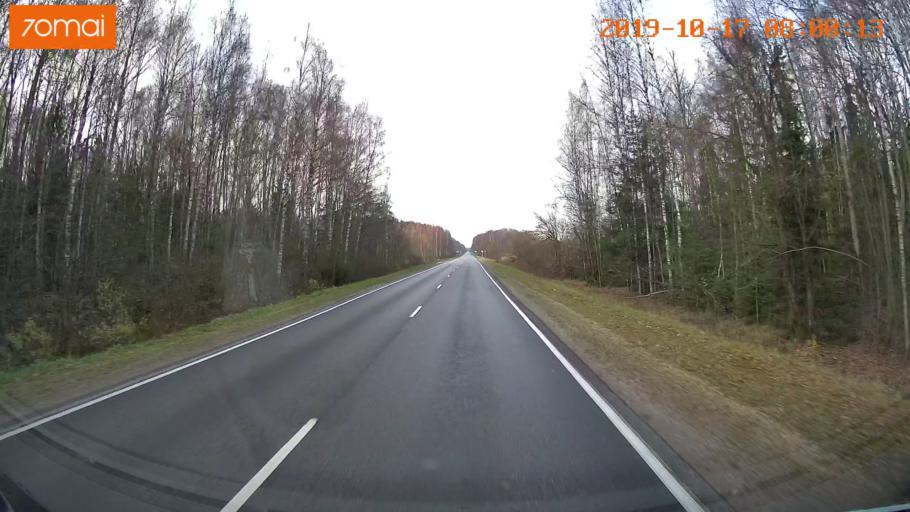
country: RU
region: Vladimir
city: Bavleny
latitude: 56.3857
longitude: 39.5227
